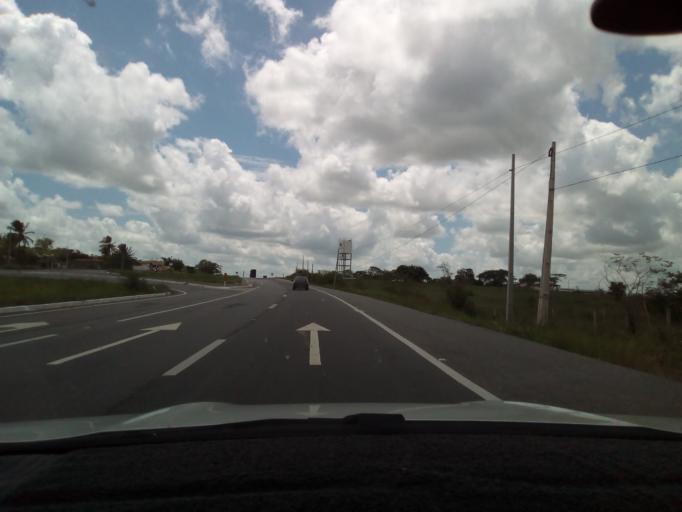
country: BR
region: Paraiba
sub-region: Gurinhem
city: Gurinhem
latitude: -7.1743
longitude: -35.3994
